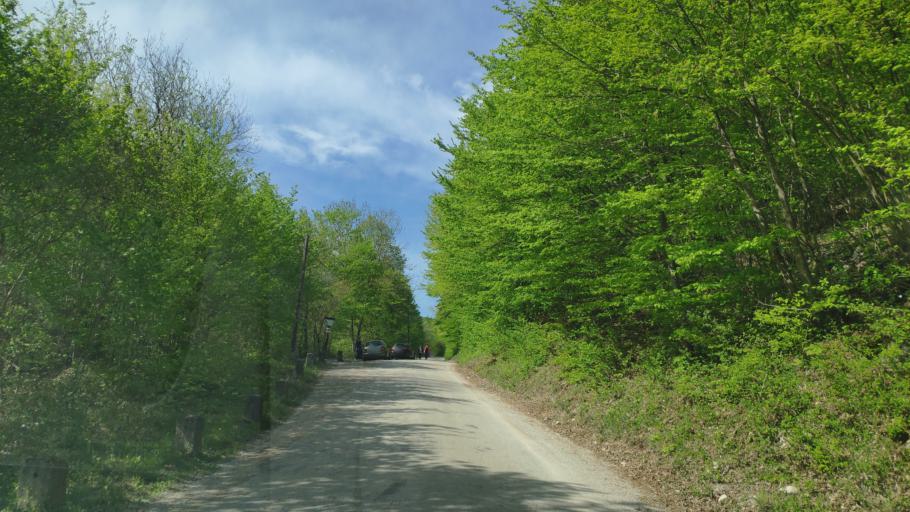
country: SK
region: Kosicky
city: Medzev
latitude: 48.6360
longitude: 20.8508
